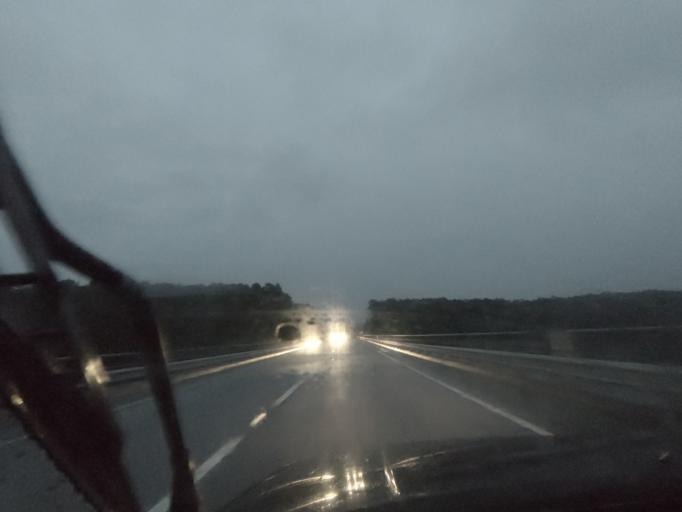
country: PT
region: Vila Real
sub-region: Vila Real
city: Vila Real
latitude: 41.2705
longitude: -7.6853
